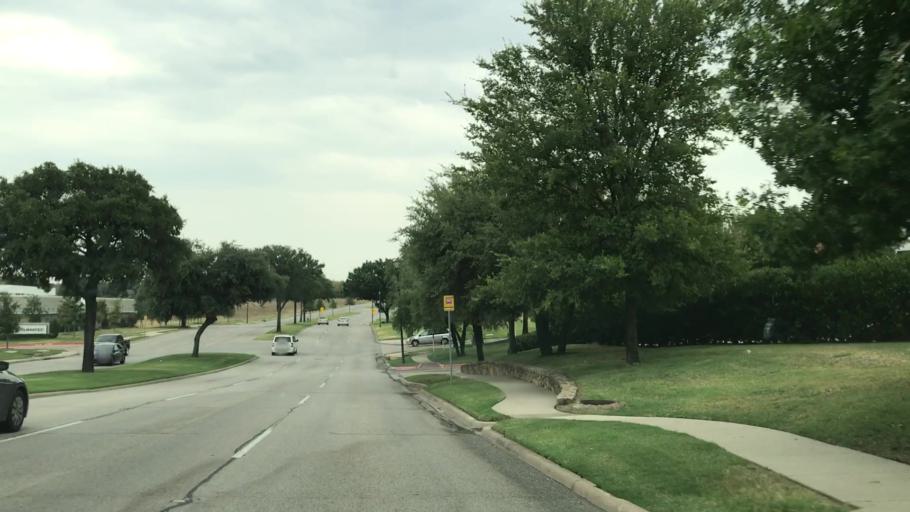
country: US
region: Texas
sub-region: Dallas County
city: Irving
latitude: 32.8783
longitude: -96.9726
